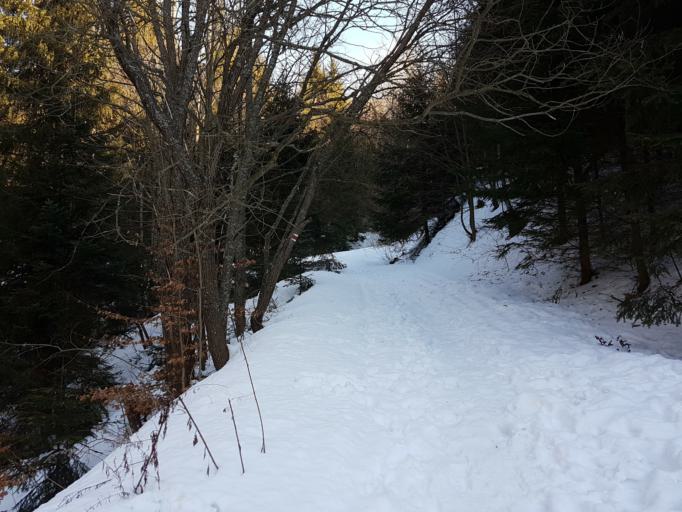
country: SK
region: Banskobystricky
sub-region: Okres Banska Bystrica
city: Banska Bystrica
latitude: 48.8113
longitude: 19.1347
